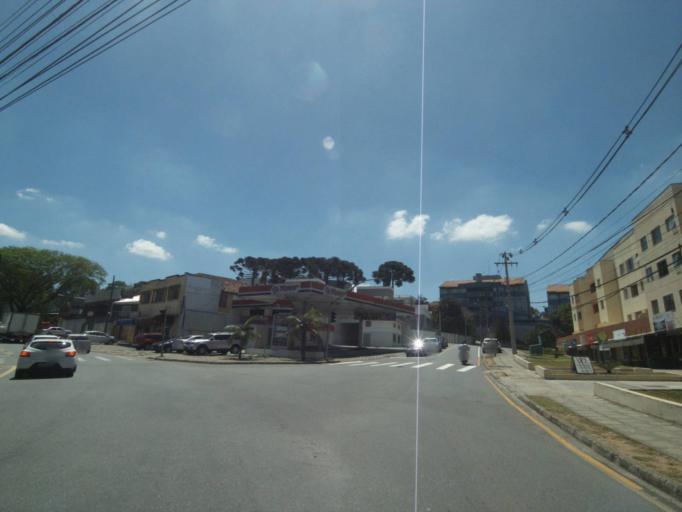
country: BR
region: Parana
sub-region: Pinhais
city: Pinhais
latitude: -25.3902
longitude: -49.2230
